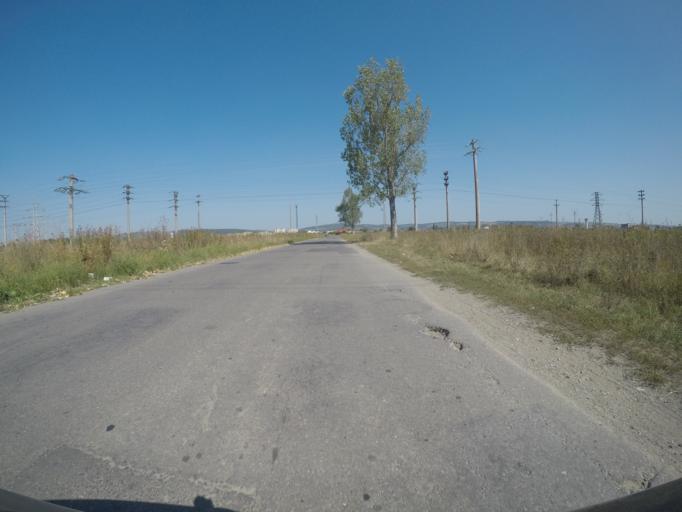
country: RO
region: Brasov
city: Fogarasch
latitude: 45.8198
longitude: 24.9803
